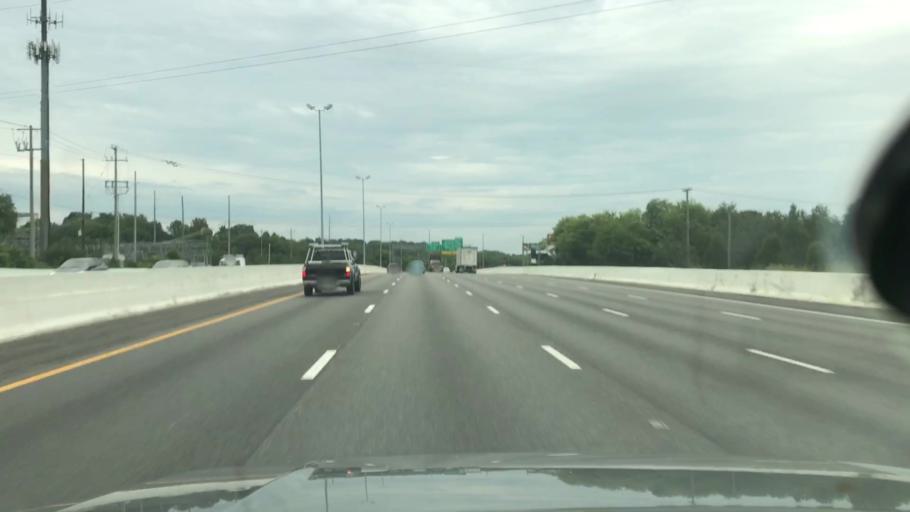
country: US
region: Tennessee
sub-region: Davidson County
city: Lakewood
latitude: 36.2277
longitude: -86.6971
